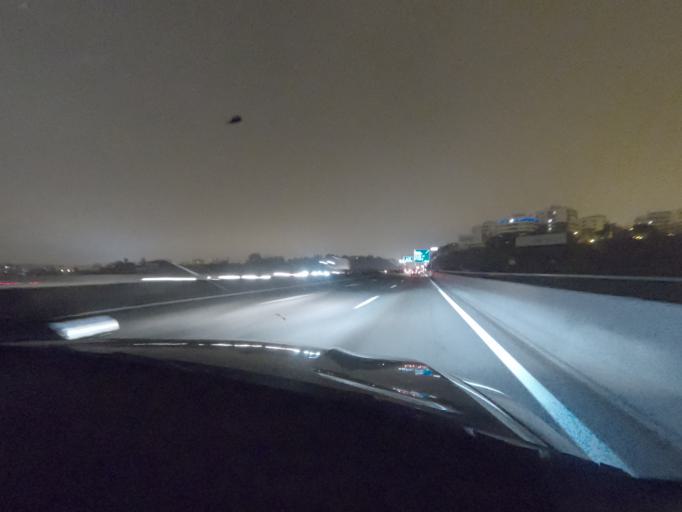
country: PT
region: Lisbon
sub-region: Loures
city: Sacavem
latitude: 38.8008
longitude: -9.1082
